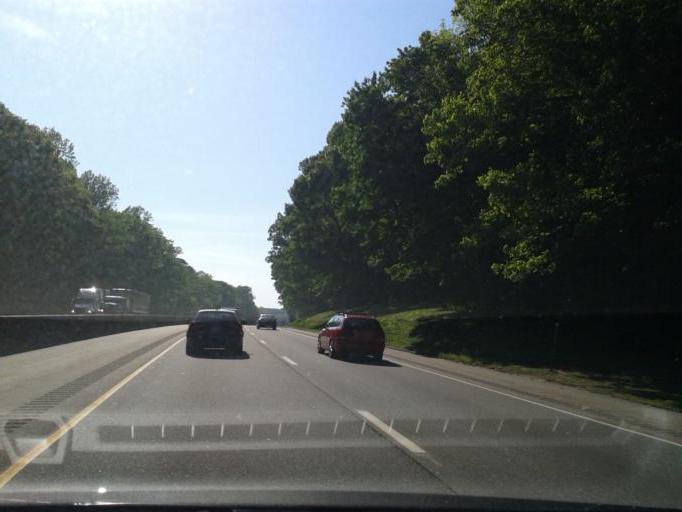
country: US
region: Connecticut
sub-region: Middlesex County
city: Westbrook Center
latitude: 41.2911
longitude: -72.4682
